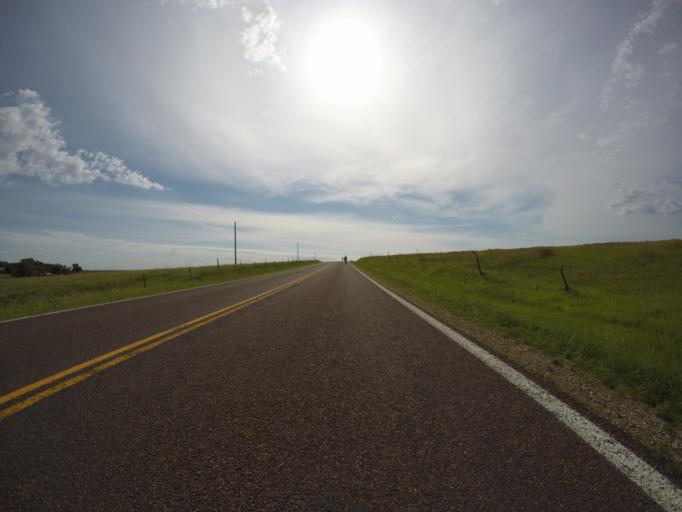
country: US
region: Kansas
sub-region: Washington County
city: Washington
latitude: 39.7124
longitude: -97.2919
